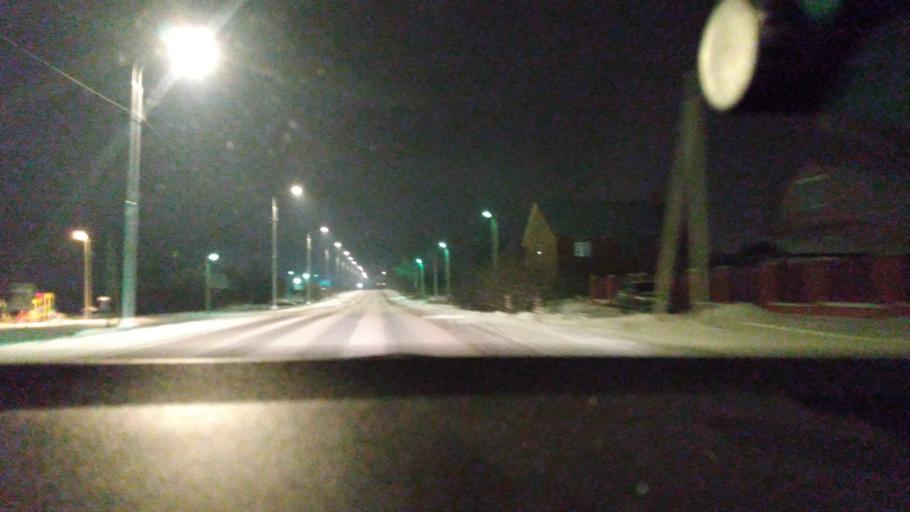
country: RU
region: Moskovskaya
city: Lukhovitsy
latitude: 55.0906
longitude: 38.9443
